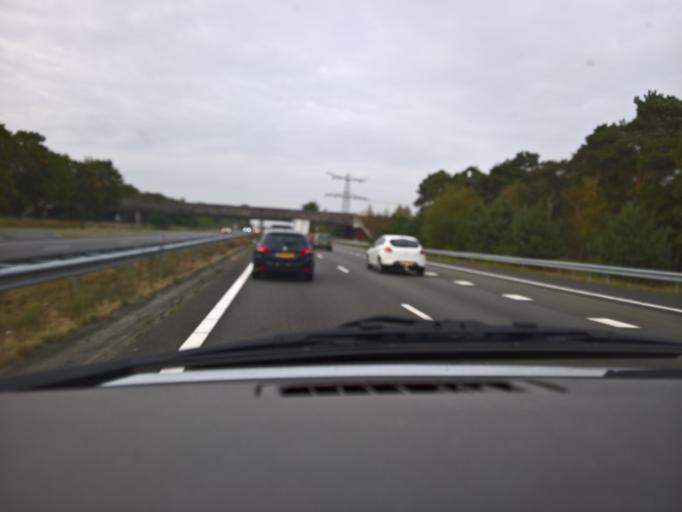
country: NL
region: North Brabant
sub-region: Gemeente Uden
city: Uden
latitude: 51.6852
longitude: 5.5890
